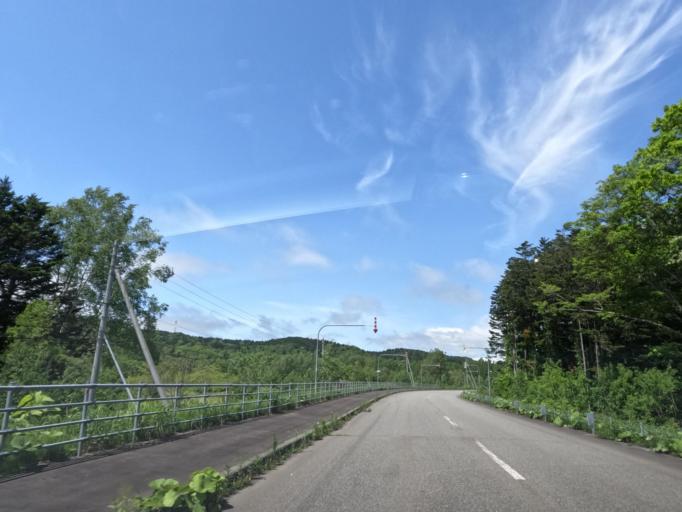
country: JP
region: Hokkaido
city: Tobetsu
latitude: 43.3782
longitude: 141.5756
